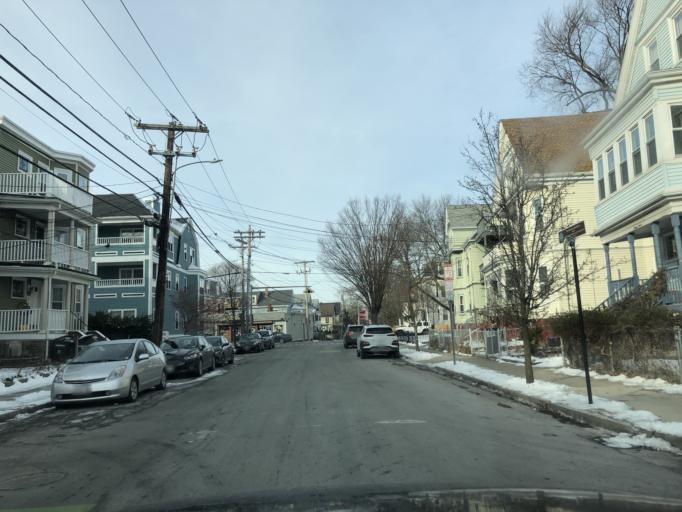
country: US
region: Massachusetts
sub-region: Middlesex County
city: Somerville
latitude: 42.3955
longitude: -71.1149
